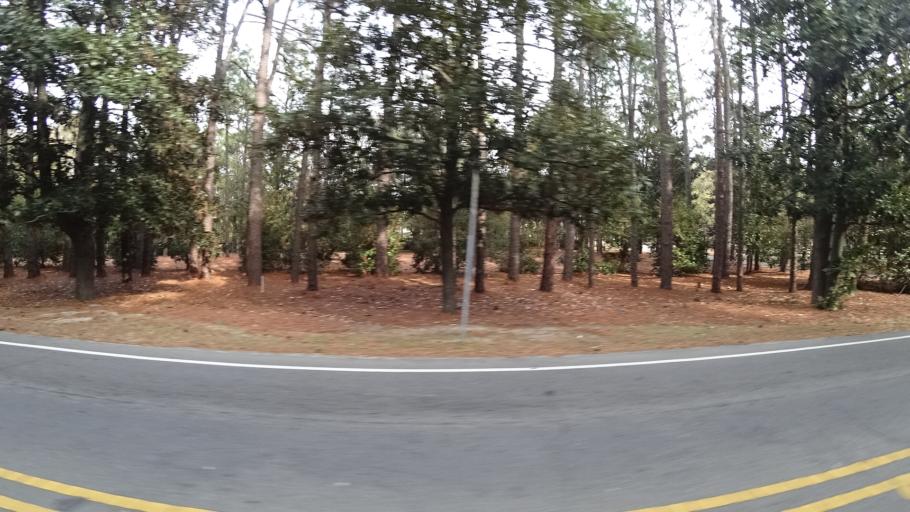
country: US
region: North Carolina
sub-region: Moore County
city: Pinehurst
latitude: 35.1923
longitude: -79.4728
